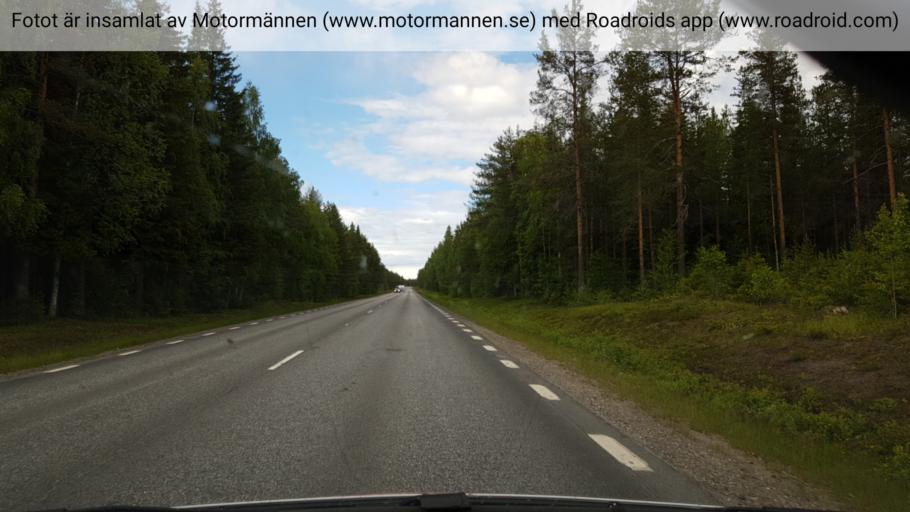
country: SE
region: Norrbotten
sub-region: Overkalix Kommun
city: OEverkalix
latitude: 66.2294
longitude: 22.8003
